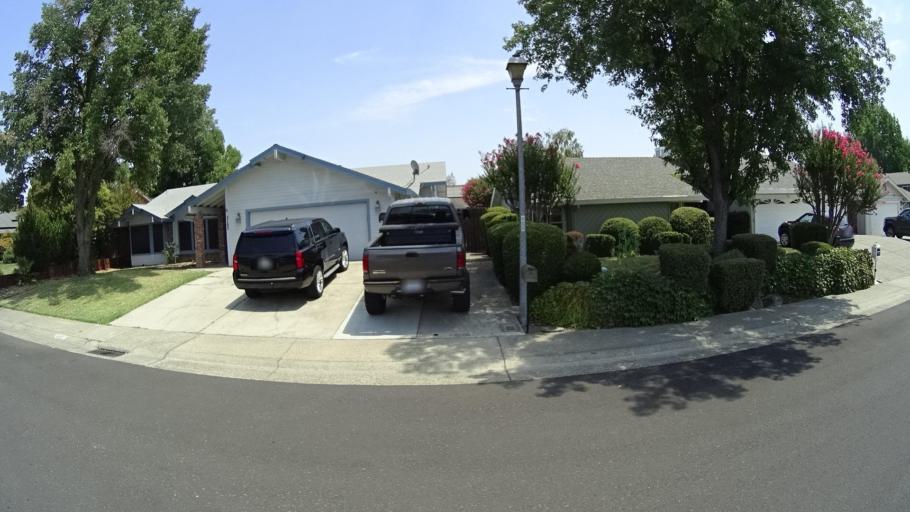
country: US
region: California
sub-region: Placer County
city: Rocklin
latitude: 38.8014
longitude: -121.2378
